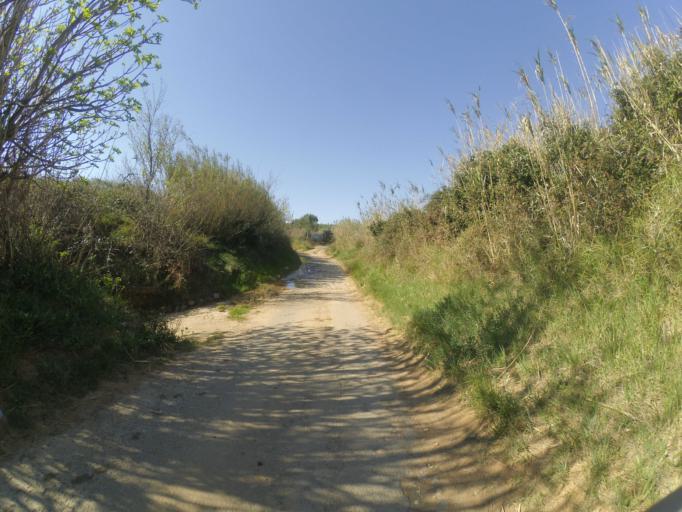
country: FR
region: Languedoc-Roussillon
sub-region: Departement des Pyrenees-Orientales
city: Baixas
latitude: 42.7448
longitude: 2.8012
